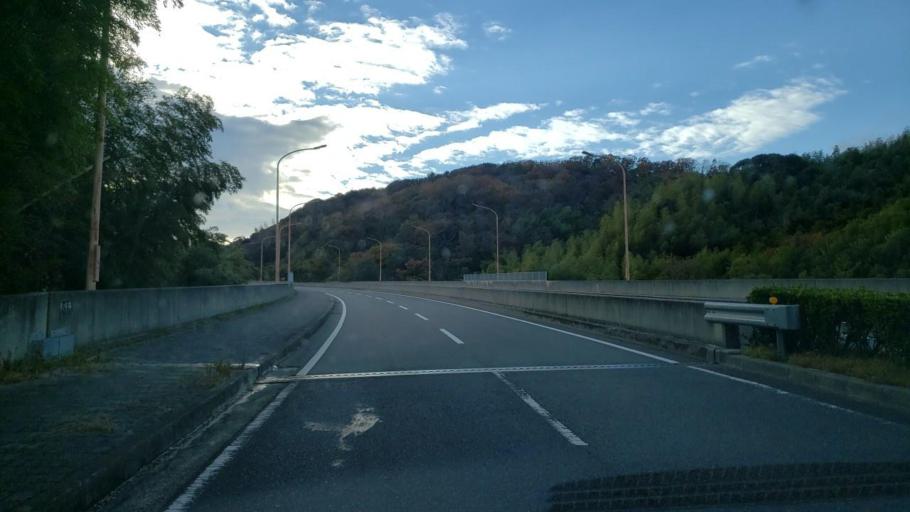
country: JP
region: Hyogo
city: Akashi
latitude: 34.5814
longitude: 135.0074
